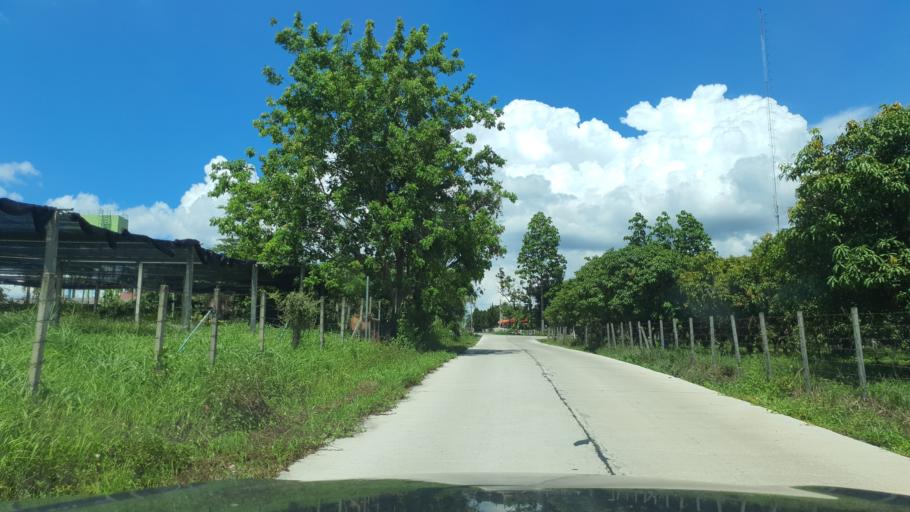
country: TH
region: Chiang Mai
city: San Sai
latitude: 18.9180
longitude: 99.0499
